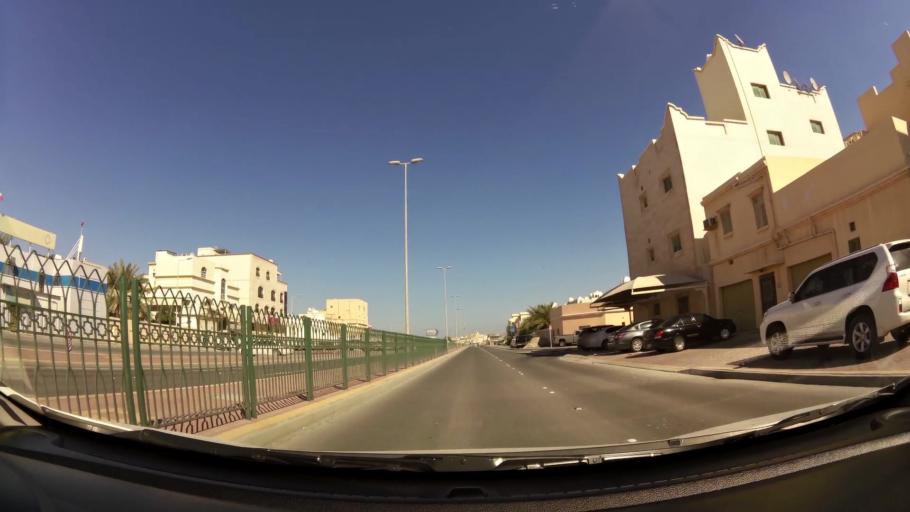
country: BH
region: Muharraq
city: Al Hadd
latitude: 26.2564
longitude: 50.6409
